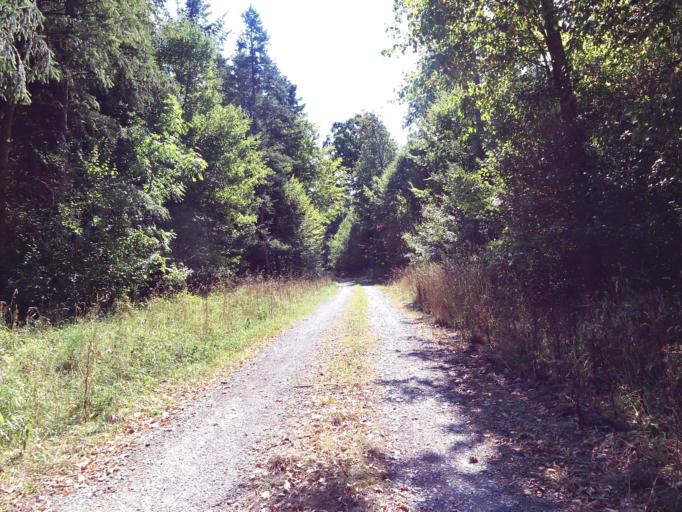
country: DE
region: Bavaria
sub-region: Regierungsbezirk Unterfranken
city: Wuerzburg
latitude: 49.7527
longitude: 9.8801
